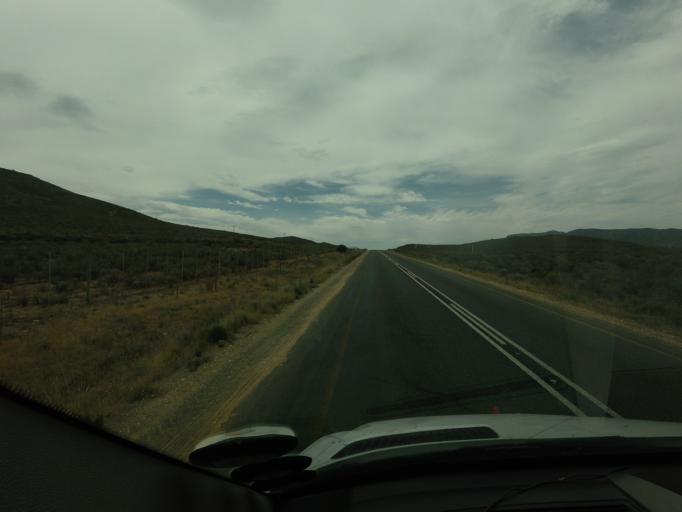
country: ZA
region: Western Cape
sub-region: Overberg District Municipality
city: Swellendam
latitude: -33.8907
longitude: 20.7314
